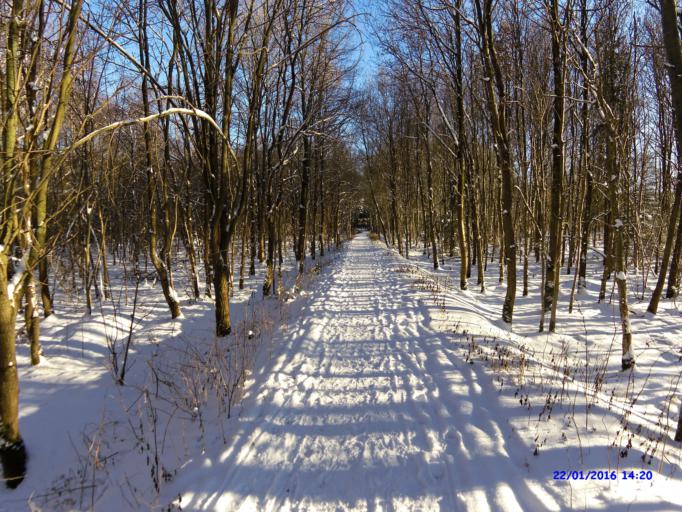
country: DE
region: Thuringia
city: Tanna
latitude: 50.4920
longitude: 11.8663
